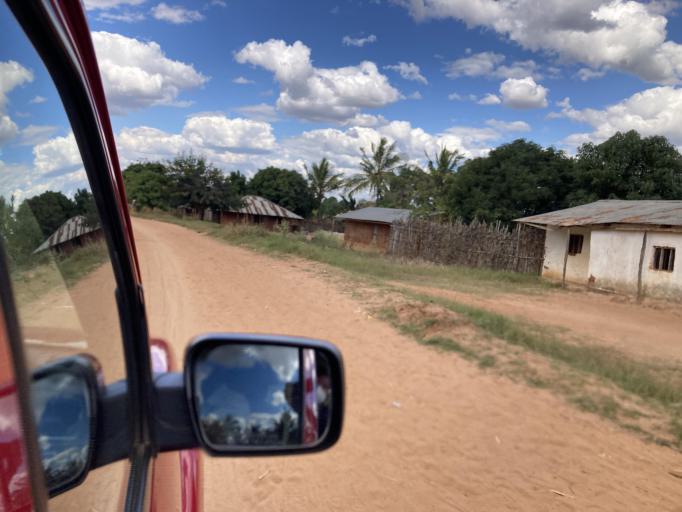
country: MZ
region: Cabo Delgado
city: Montepuez
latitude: -13.1253
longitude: 39.0287
